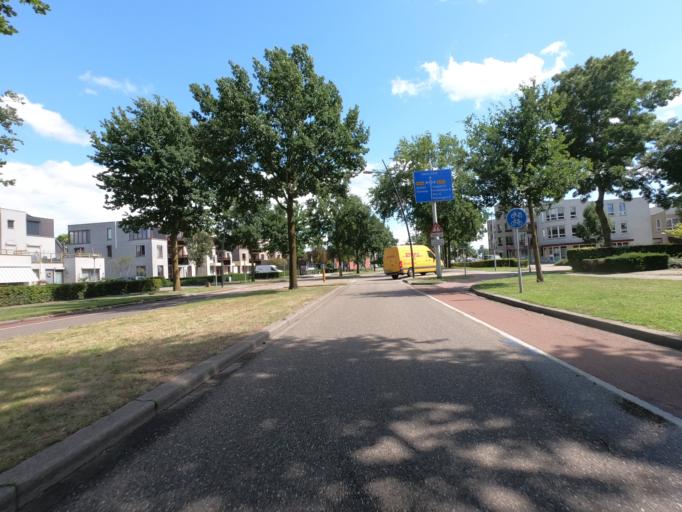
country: NL
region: North Brabant
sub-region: Gemeente Uden
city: Uden
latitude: 51.6500
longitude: 5.6233
